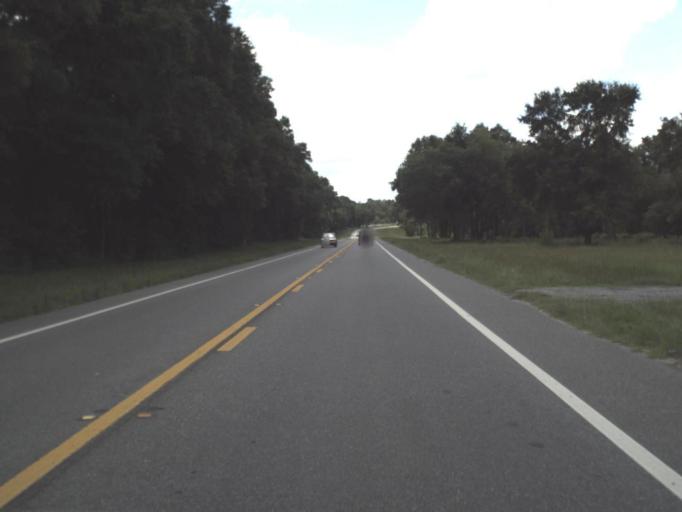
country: US
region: Florida
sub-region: Suwannee County
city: Wellborn
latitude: 30.3170
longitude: -82.7214
